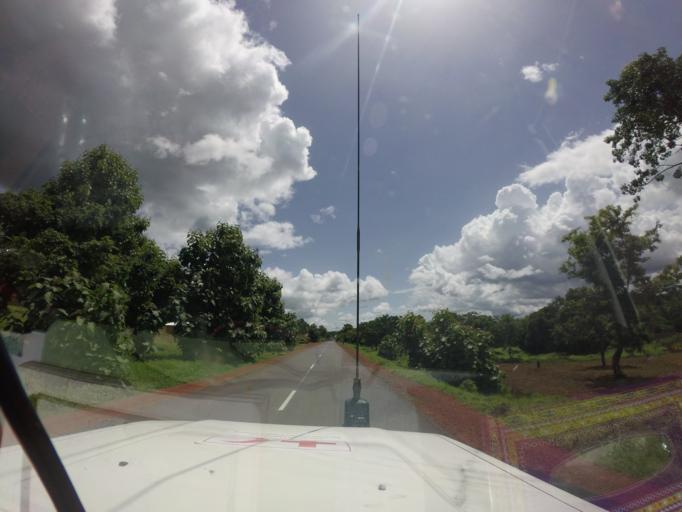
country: SL
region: Northern Province
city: Bindi
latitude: 10.1470
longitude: -11.5976
